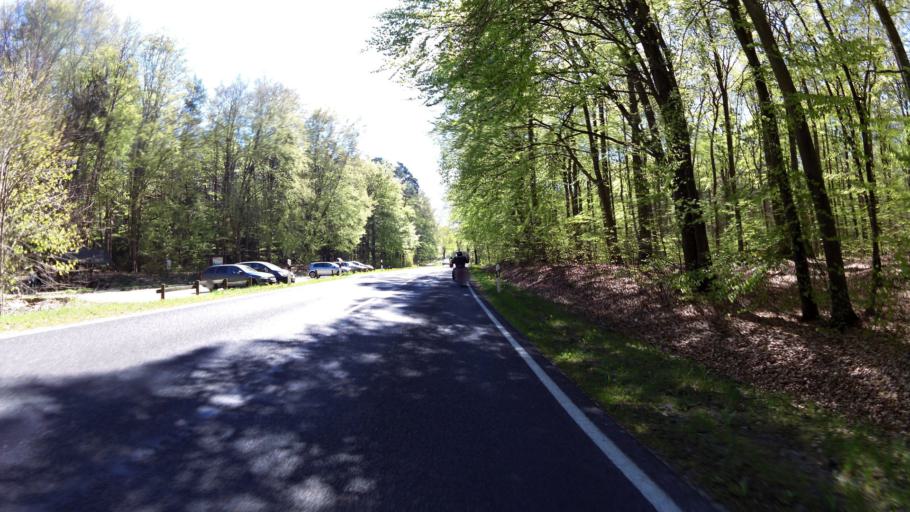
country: DE
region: Brandenburg
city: Wandlitz
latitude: 52.7244
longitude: 13.5129
